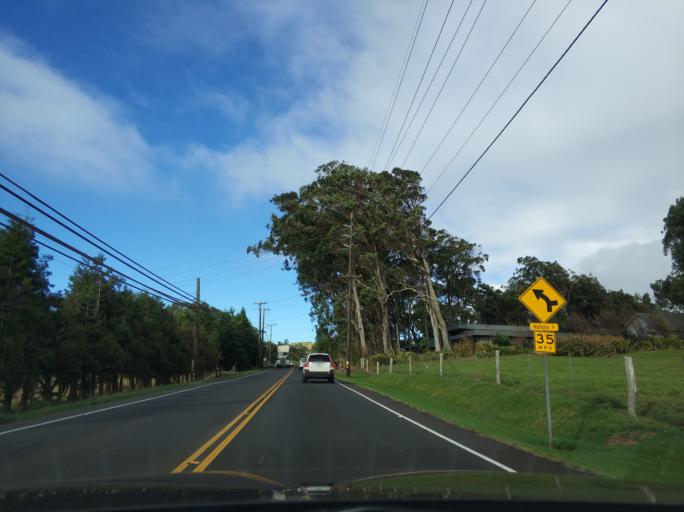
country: US
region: Hawaii
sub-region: Hawaii County
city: Waimea
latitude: 20.0351
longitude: -155.6312
